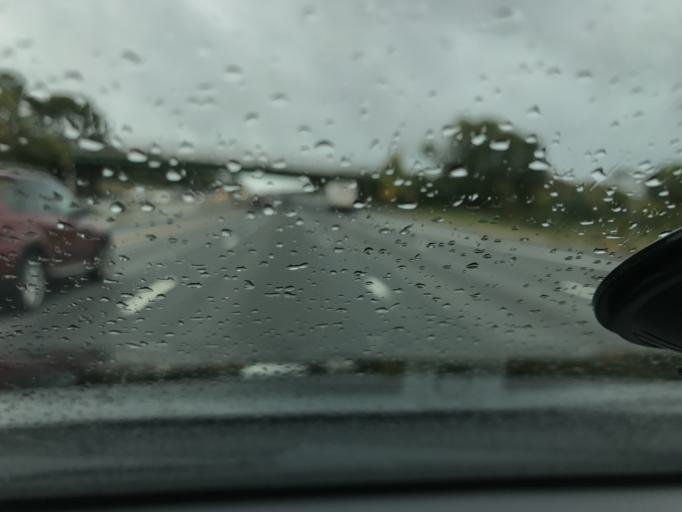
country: US
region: Massachusetts
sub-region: Middlesex County
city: Waltham
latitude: 42.3713
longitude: -71.2692
